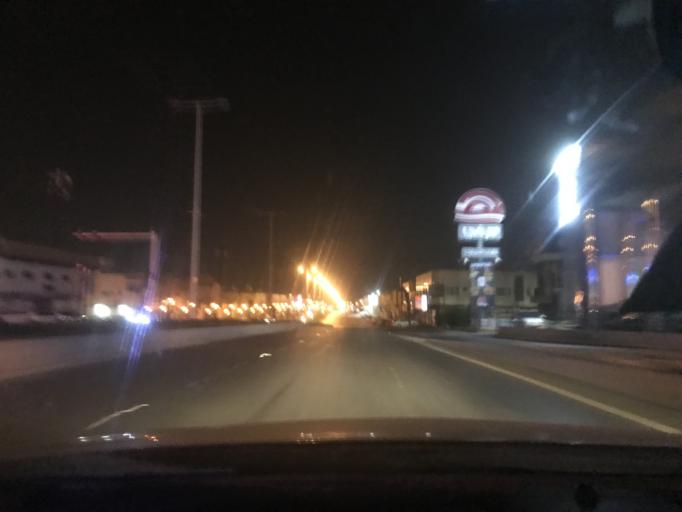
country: SA
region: Ar Riyad
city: Riyadh
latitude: 24.7402
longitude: 46.7493
